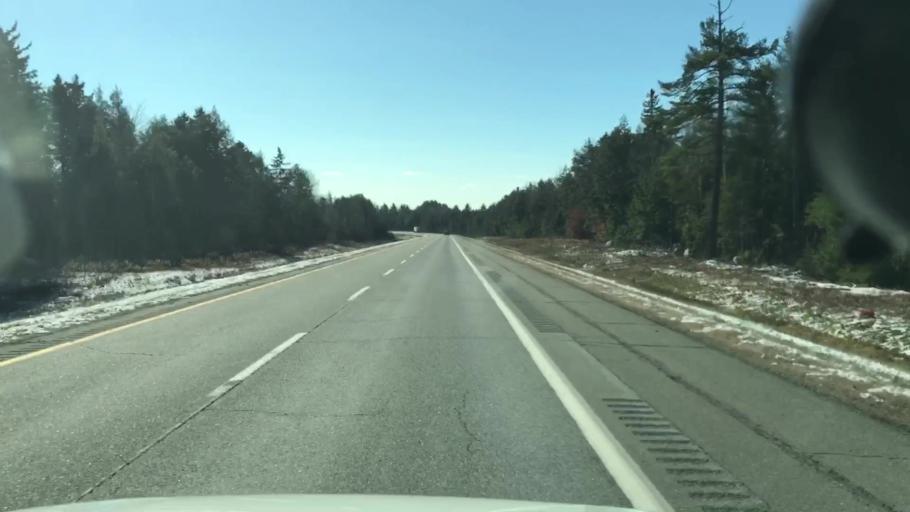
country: US
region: Maine
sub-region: Penobscot County
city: Howland
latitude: 45.2763
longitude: -68.6754
